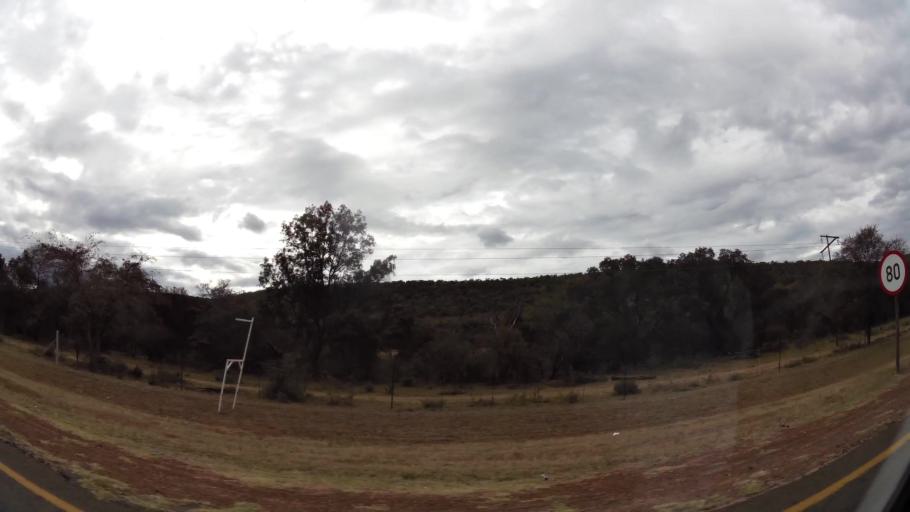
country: ZA
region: Limpopo
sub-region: Waterberg District Municipality
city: Modimolle
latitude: -24.6663
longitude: 28.4676
